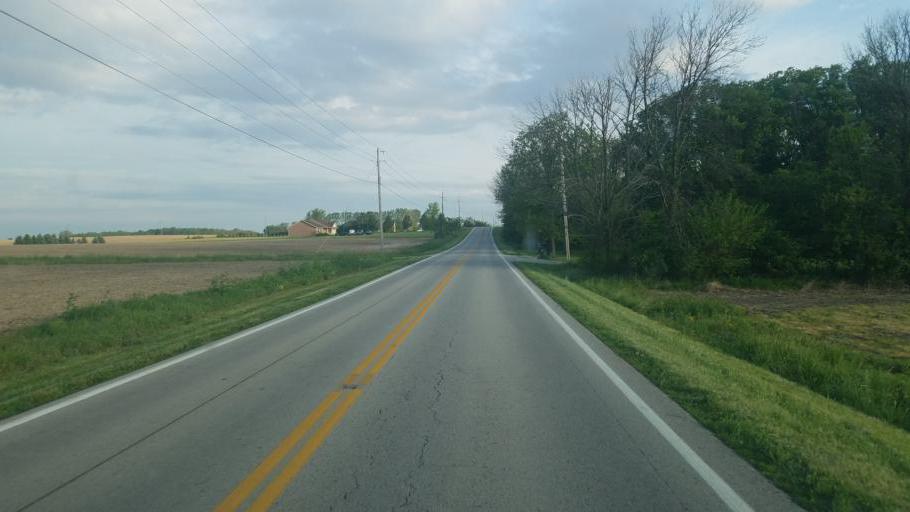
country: US
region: Ohio
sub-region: Clinton County
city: Sabina
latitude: 39.4622
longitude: -83.6604
